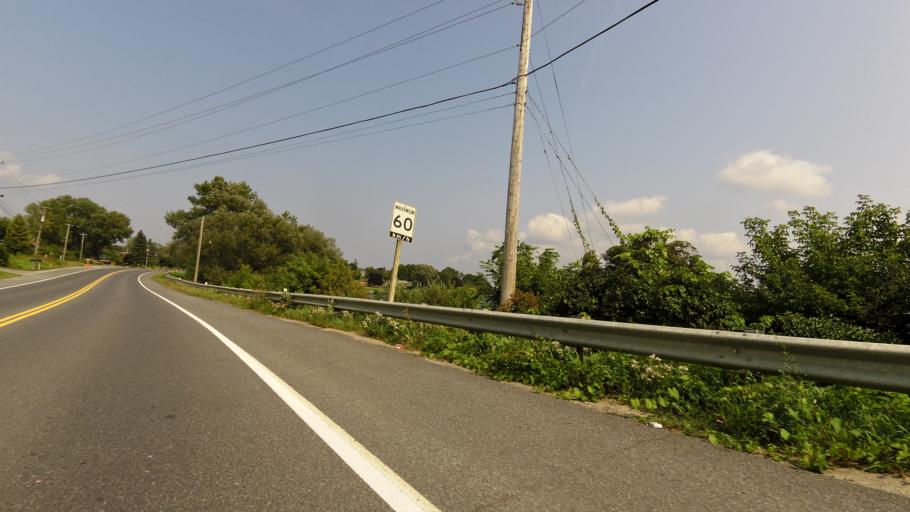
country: CA
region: Ontario
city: Prescott
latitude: 44.7017
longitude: -75.5284
